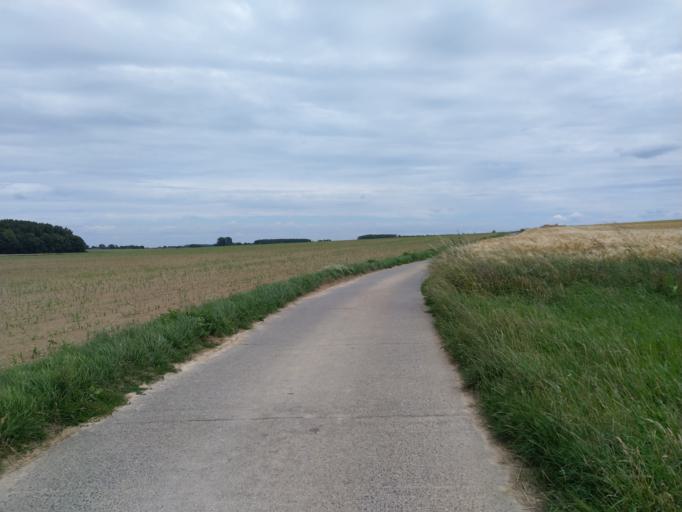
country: BE
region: Wallonia
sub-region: Province du Hainaut
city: Beloeil
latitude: 50.5420
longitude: 3.7805
